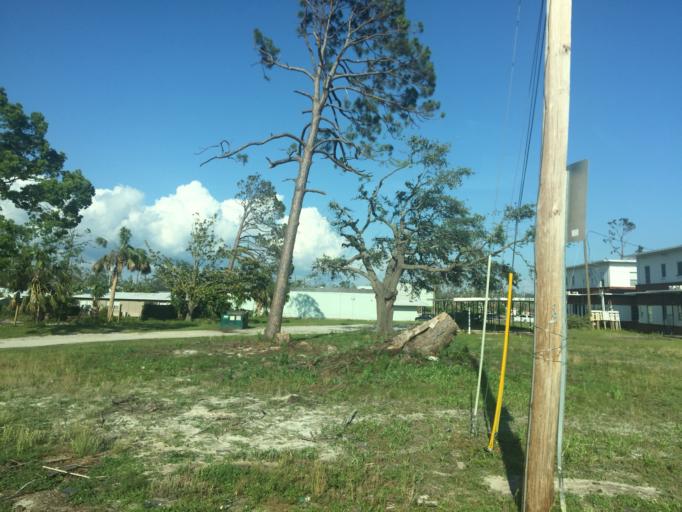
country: US
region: Florida
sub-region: Bay County
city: Panama City
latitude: 30.1465
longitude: -85.6492
